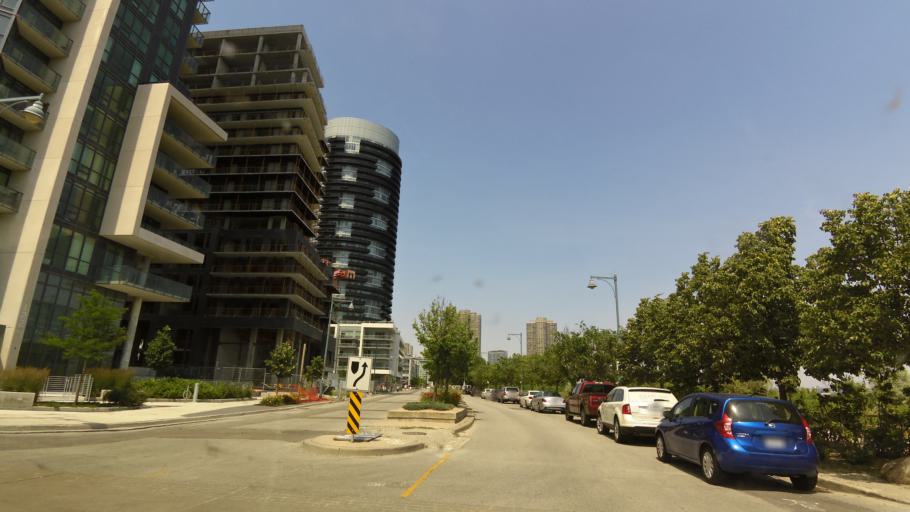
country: CA
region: Ontario
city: Etobicoke
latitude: 43.6245
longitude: -79.4776
